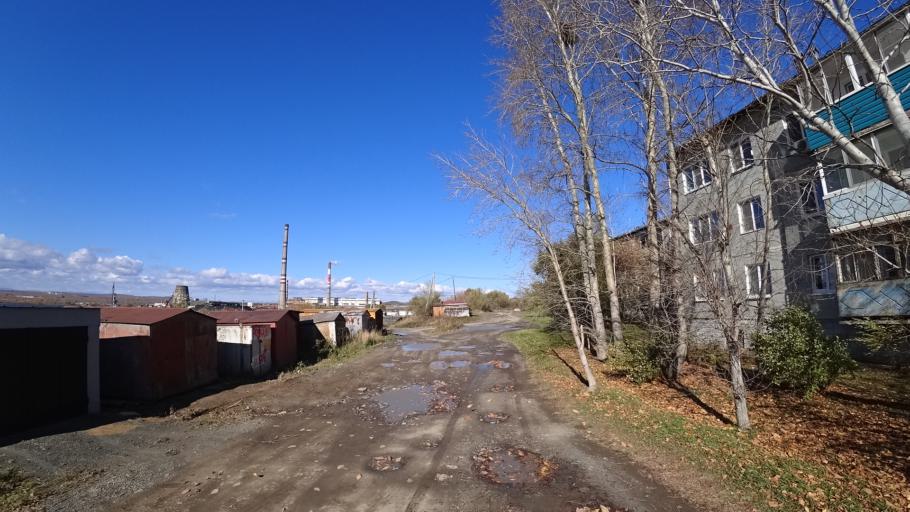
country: RU
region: Khabarovsk Krai
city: Amursk
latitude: 50.2162
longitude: 136.8890
